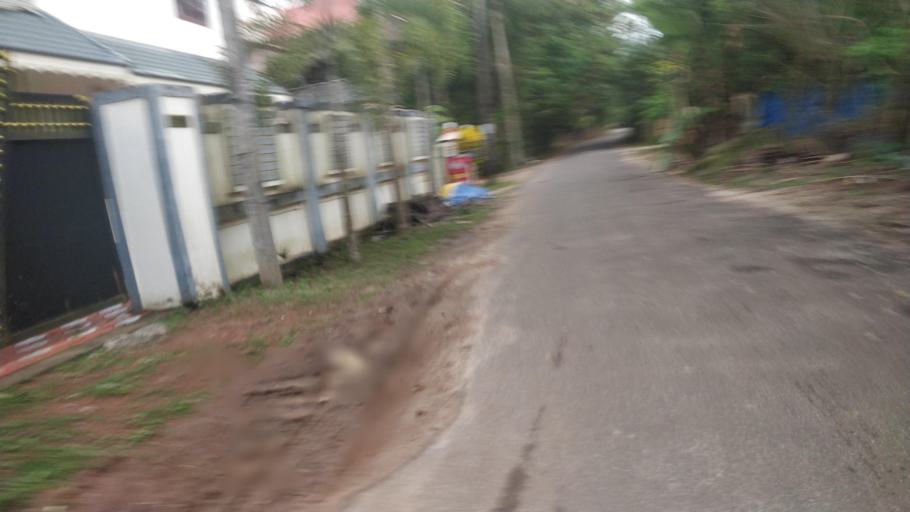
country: IN
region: Kerala
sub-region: Alappuzha
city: Vayalar
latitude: 9.7088
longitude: 76.3493
